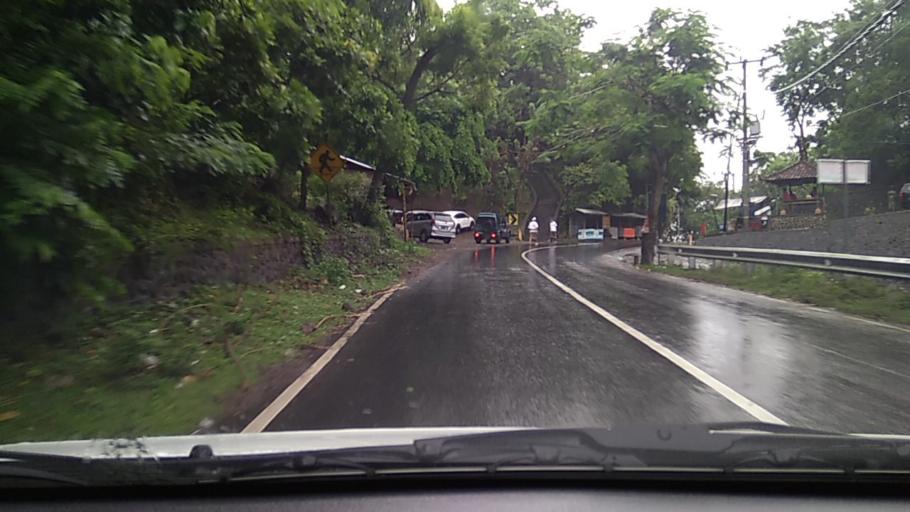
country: ID
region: Bali
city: Banjar Bugbug
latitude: -8.4959
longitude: 115.5860
